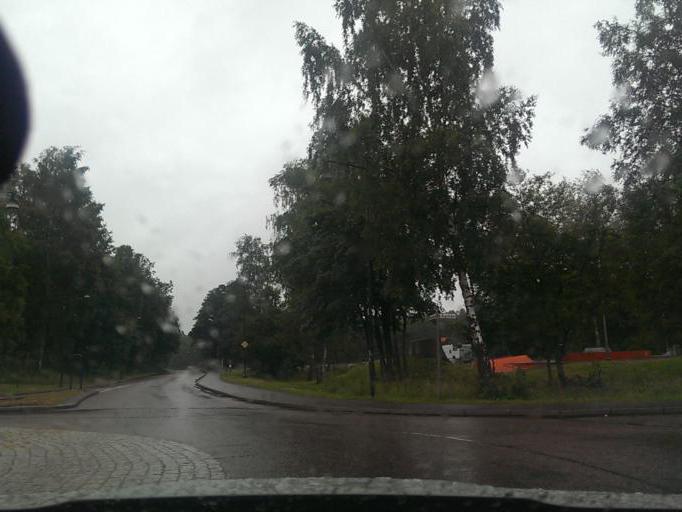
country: SE
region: Skane
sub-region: Orkelljunga Kommun
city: OErkelljunga
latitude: 56.2831
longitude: 13.2849
